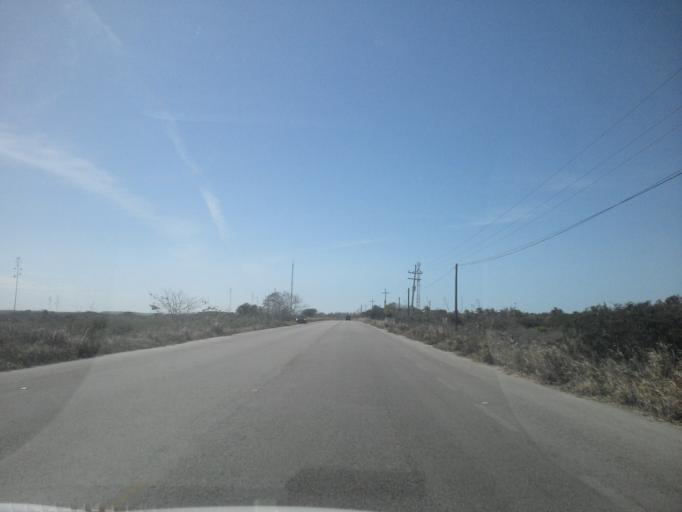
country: MX
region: Yucatan
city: Telchac Puerto
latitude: 21.3289
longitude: -89.3873
